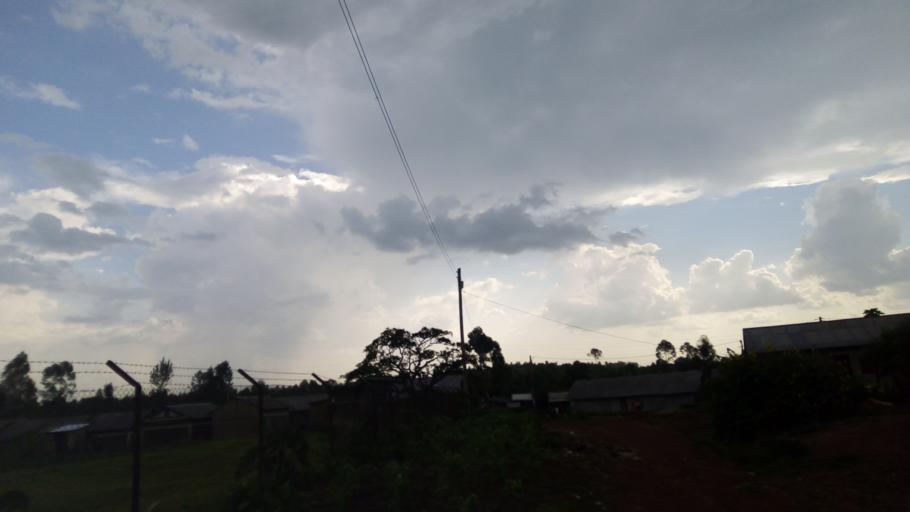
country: UG
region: Eastern Region
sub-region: Mbale District
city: Mbale
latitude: 1.0679
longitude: 34.1602
